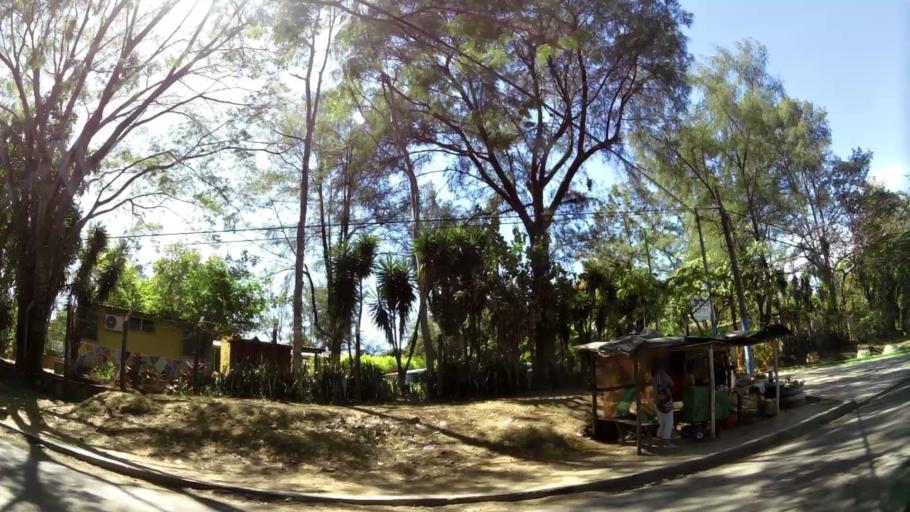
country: SV
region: Ahuachapan
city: Ahuachapan
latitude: 13.9372
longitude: -89.8581
